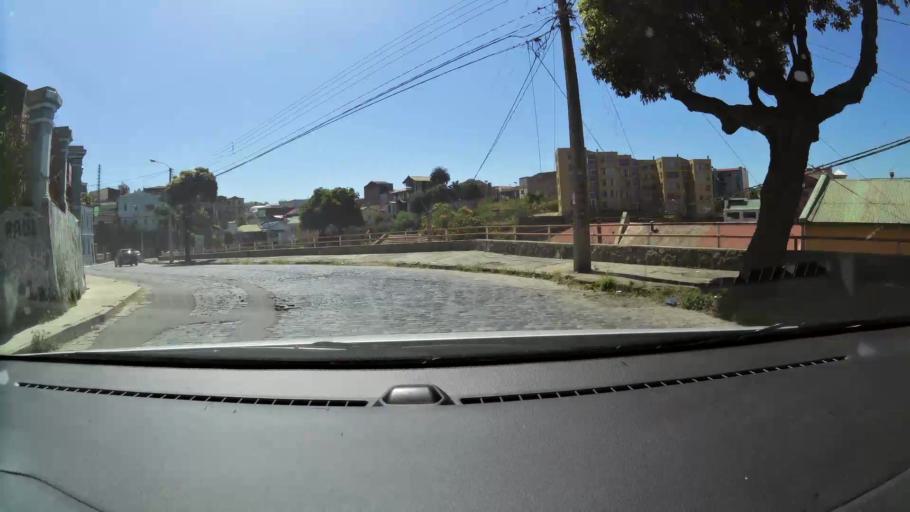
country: CL
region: Valparaiso
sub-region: Provincia de Valparaiso
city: Valparaiso
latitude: -33.0307
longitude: -71.6336
